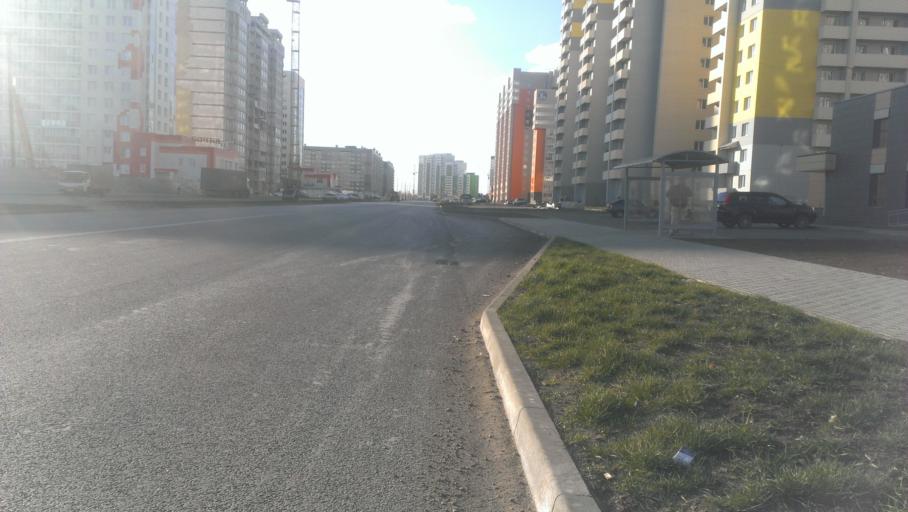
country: RU
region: Altai Krai
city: Novosilikatnyy
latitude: 53.3370
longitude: 83.6604
